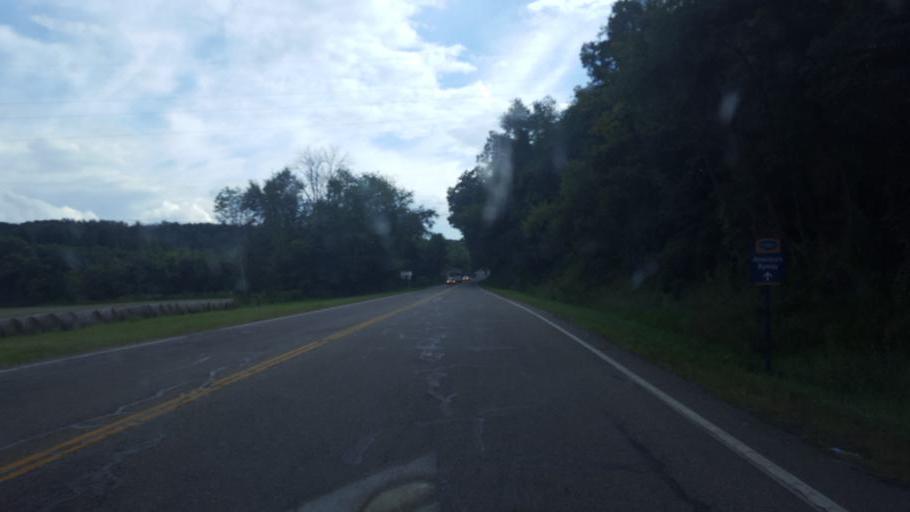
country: US
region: Ohio
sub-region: Tuscarawas County
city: Dover
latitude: 40.5302
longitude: -81.4327
